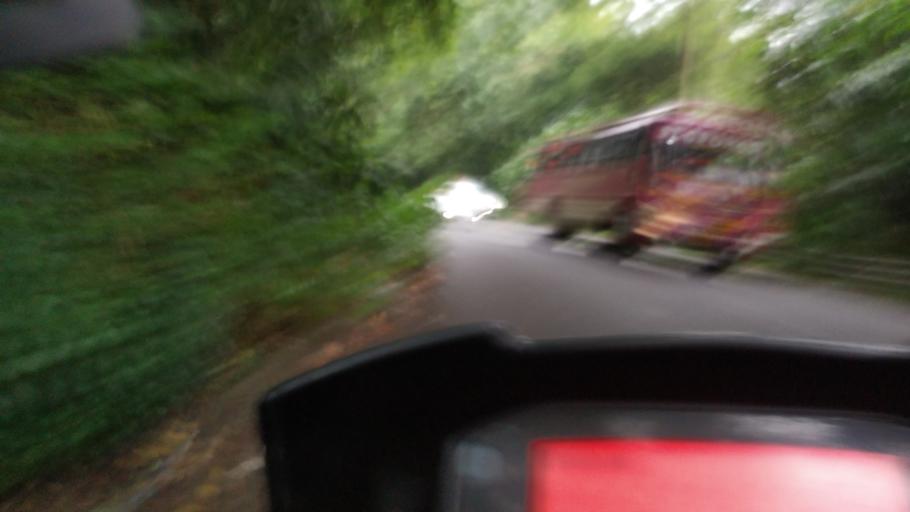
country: IN
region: Kerala
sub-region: Idukki
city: Kuttampuzha
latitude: 10.0647
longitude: 76.7948
